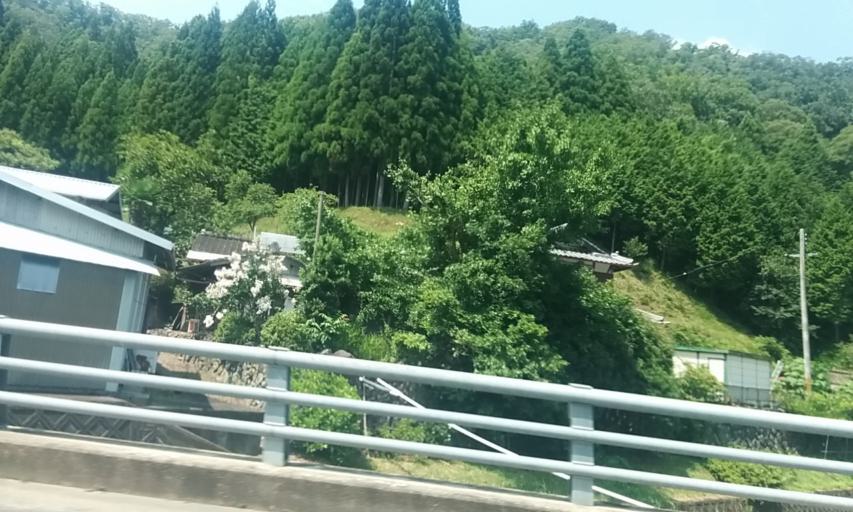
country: JP
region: Kyoto
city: Ayabe
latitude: 35.2141
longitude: 135.2083
